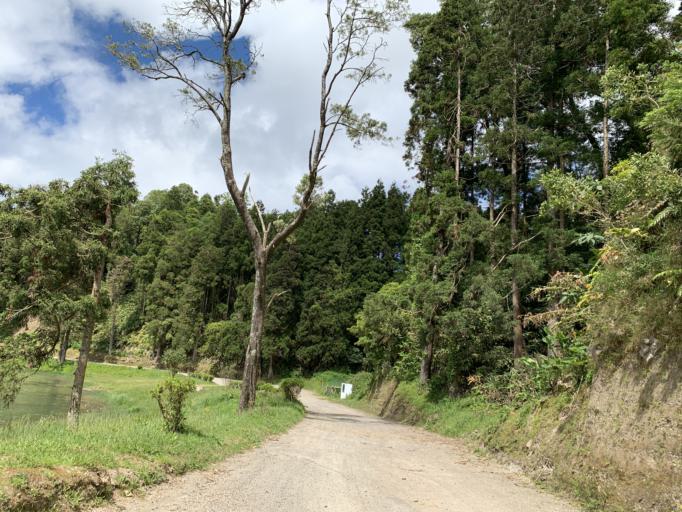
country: PT
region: Azores
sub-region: Ponta Delgada
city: Arrifes
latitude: 37.8530
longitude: -25.7854
